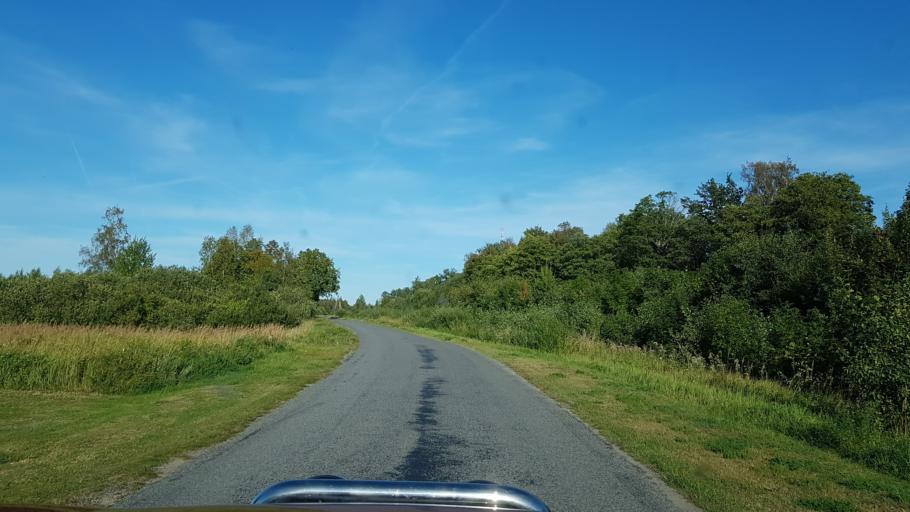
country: LV
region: Salacgrivas
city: Ainazi
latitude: 57.8763
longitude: 24.3726
